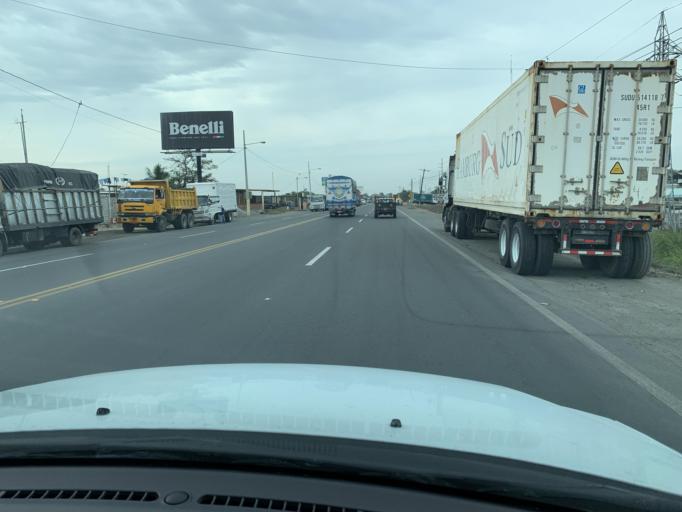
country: EC
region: Guayas
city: Yaguachi Nuevo
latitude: -2.2438
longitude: -79.6368
